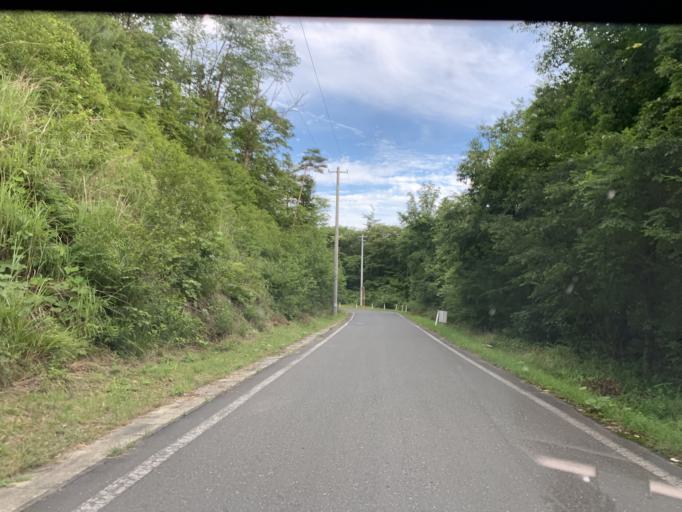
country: JP
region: Iwate
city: Ichinoseki
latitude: 38.9129
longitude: 141.0352
